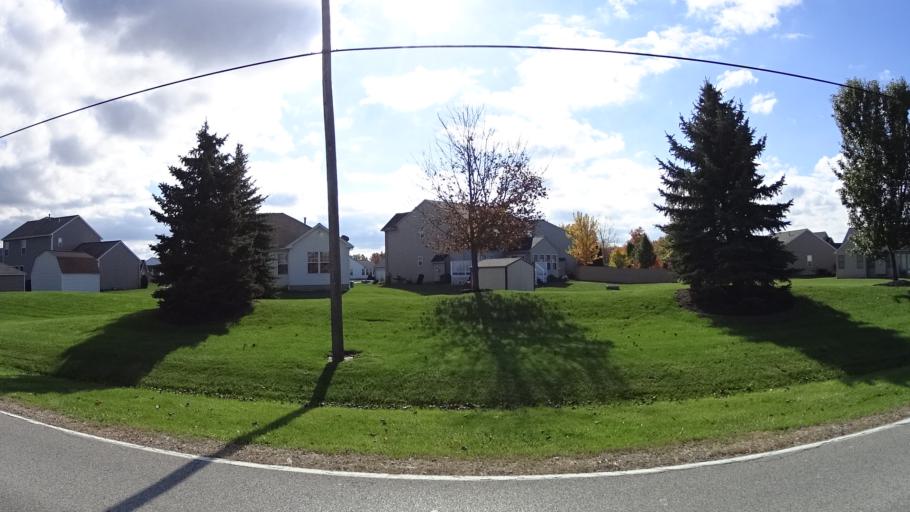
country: US
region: Ohio
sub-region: Lorain County
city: Lorain
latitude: 41.4418
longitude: -82.2210
